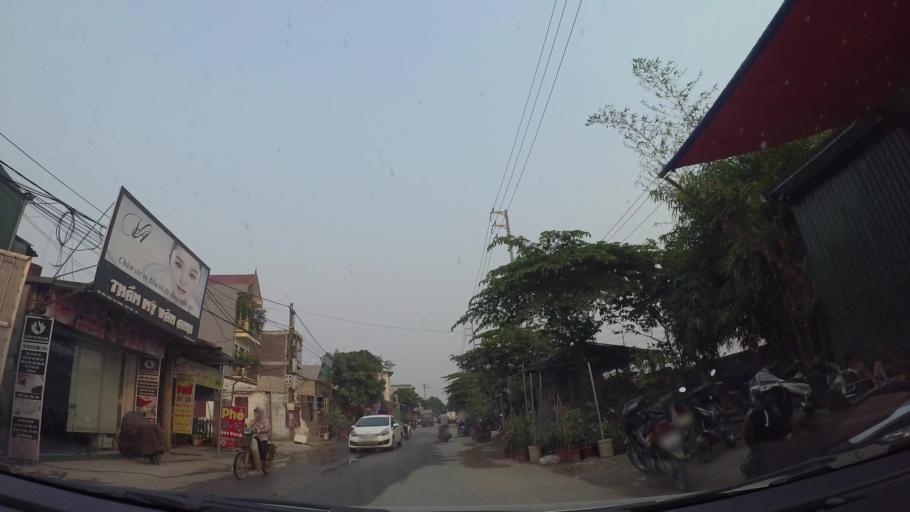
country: VN
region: Ha Noi
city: Cau Dien
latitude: 21.0043
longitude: 105.7214
